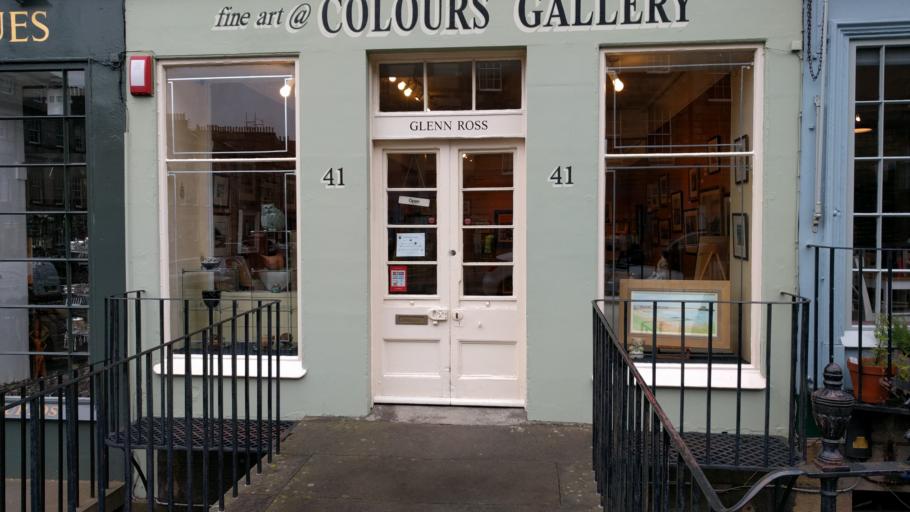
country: GB
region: Scotland
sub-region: Edinburgh
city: Edinburgh
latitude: 55.9577
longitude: -3.1993
